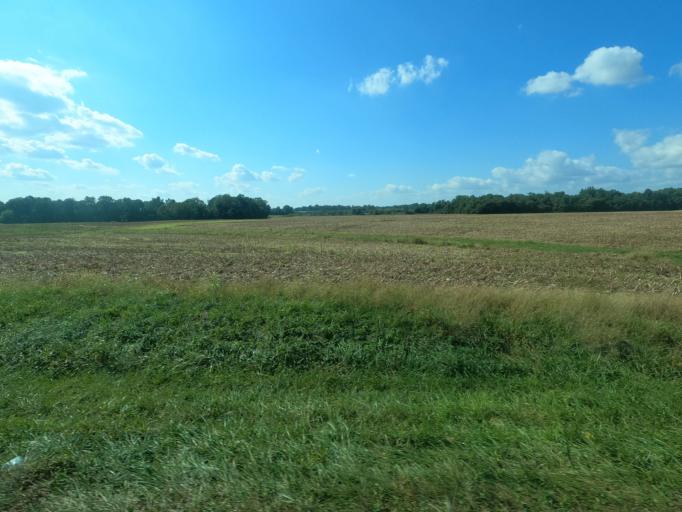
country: US
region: Illinois
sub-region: Massac County
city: Metropolis
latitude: 37.2105
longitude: -88.7291
